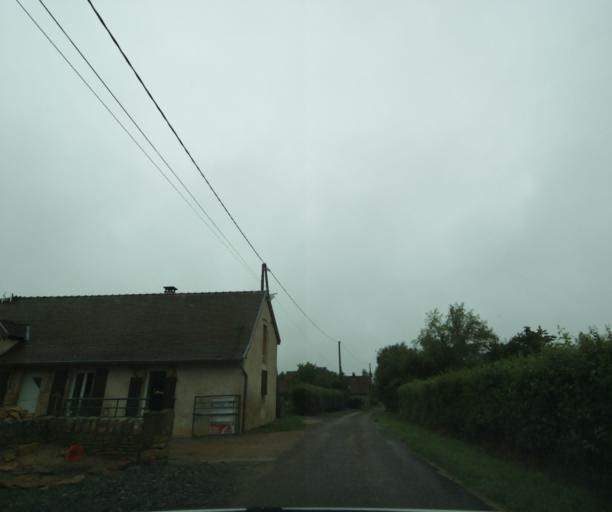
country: FR
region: Bourgogne
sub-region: Departement de Saone-et-Loire
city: Paray-le-Monial
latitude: 46.4028
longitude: 4.1915
